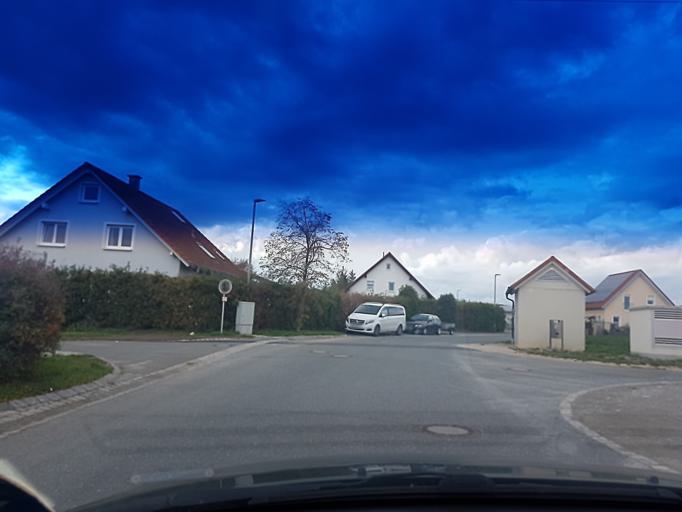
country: DE
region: Bavaria
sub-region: Regierungsbezirk Mittelfranken
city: Muhlhausen
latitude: 49.7518
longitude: 10.7656
